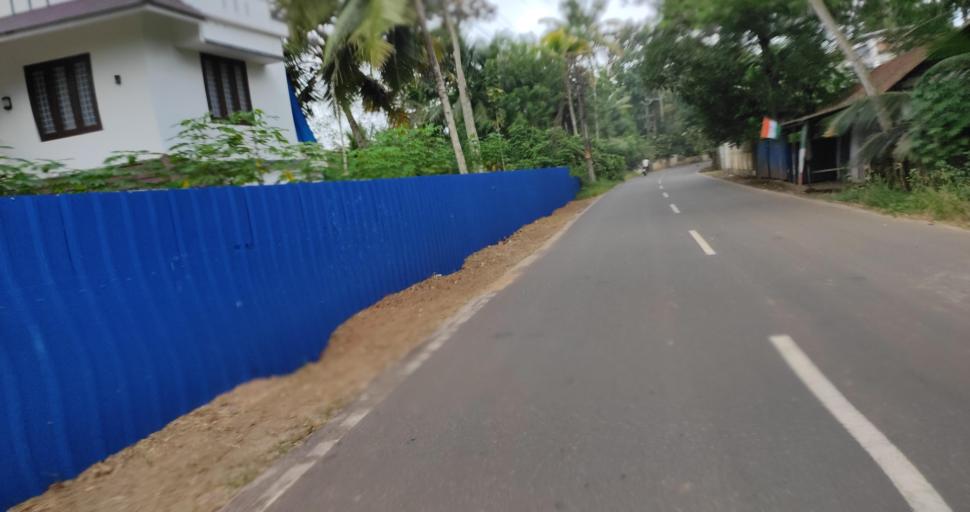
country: IN
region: Kerala
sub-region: Alappuzha
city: Shertallai
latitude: 9.6533
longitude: 76.3143
